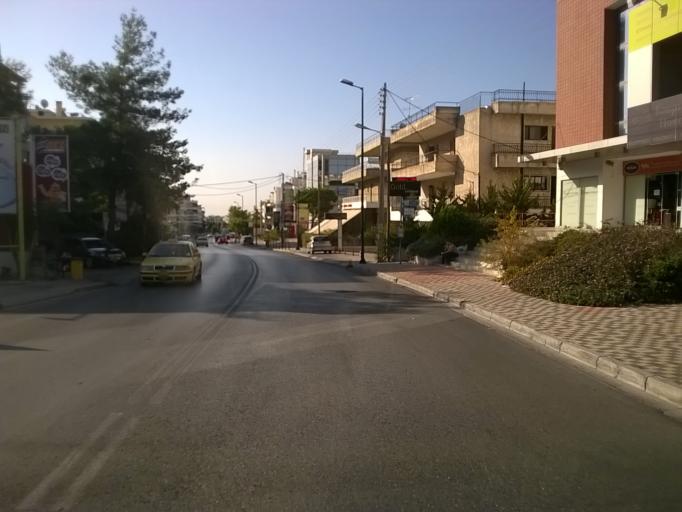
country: GR
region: Attica
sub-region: Nomarchia Athinas
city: Glyfada
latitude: 37.8787
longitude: 23.7635
